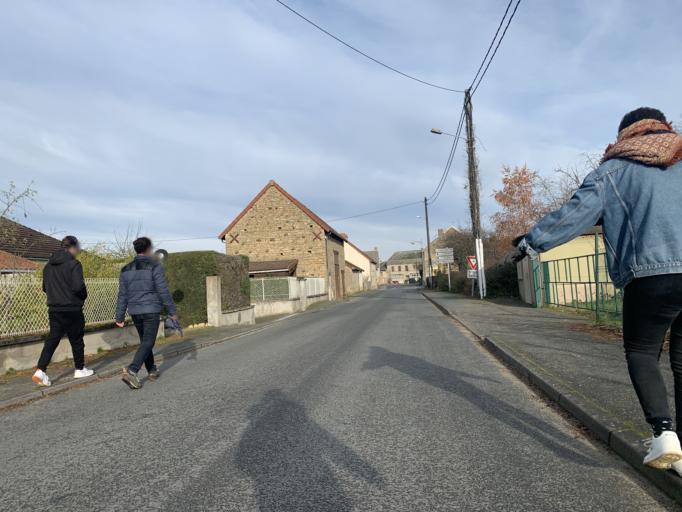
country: FR
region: Limousin
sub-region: Departement de la Creuse
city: Ajain
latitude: 46.2060
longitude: 1.9992
